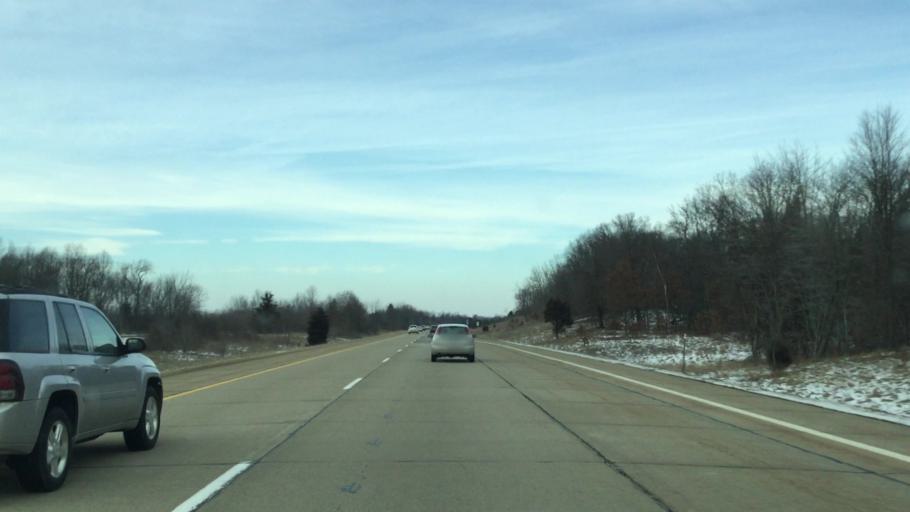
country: US
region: Michigan
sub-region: Calhoun County
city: Marshall
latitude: 42.3568
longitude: -84.9810
